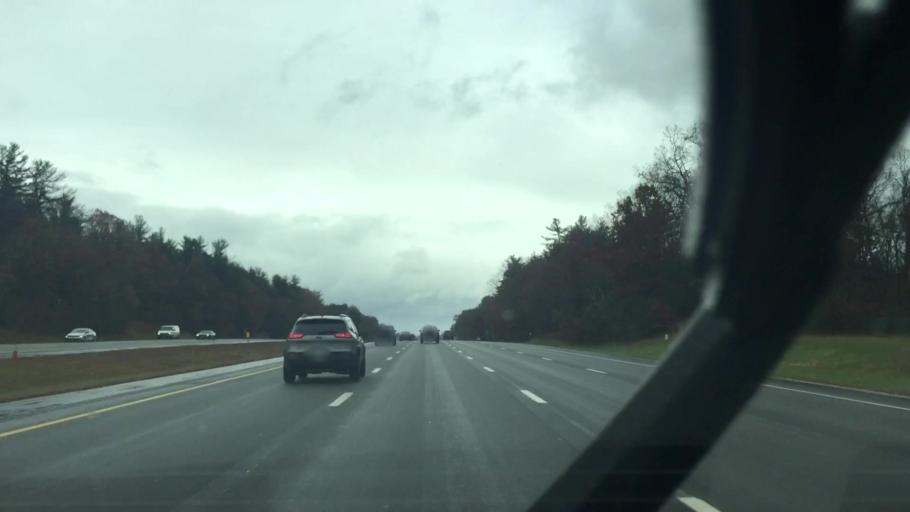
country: US
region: New Hampshire
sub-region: Rockingham County
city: Seabrook
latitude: 42.9077
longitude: -70.8761
